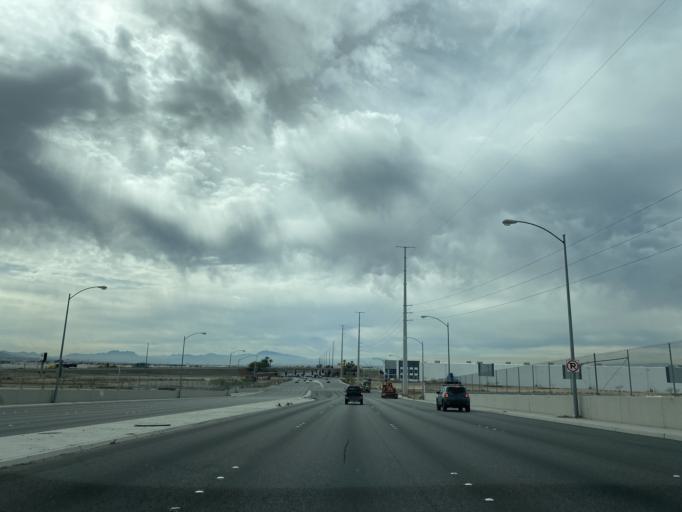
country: US
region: Nevada
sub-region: Clark County
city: Nellis Air Force Base
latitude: 36.2641
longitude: -115.0799
